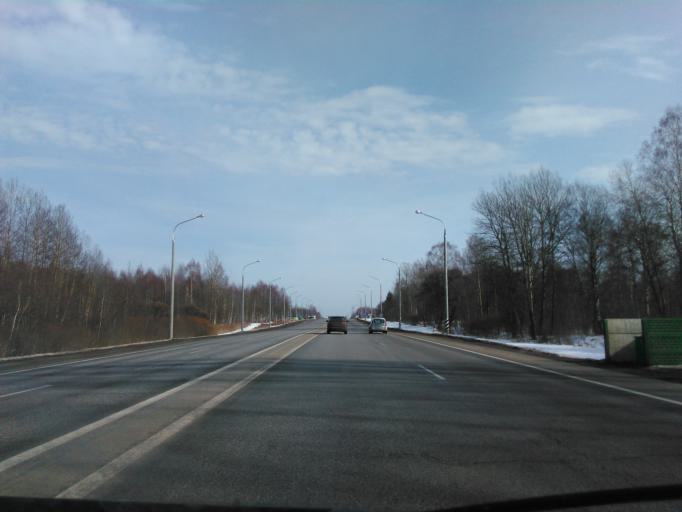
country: RU
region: Smolensk
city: Rudnya
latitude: 54.6903
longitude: 30.9607
